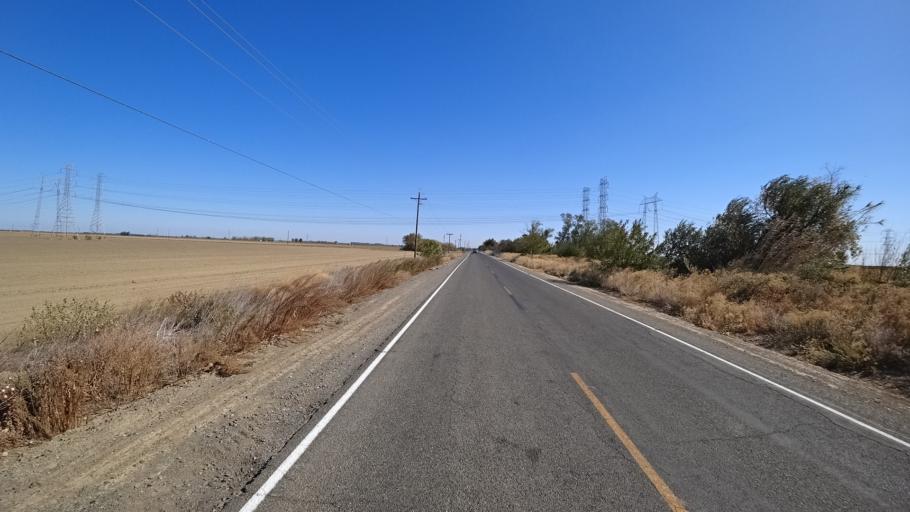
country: US
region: California
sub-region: Yolo County
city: Winters
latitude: 38.5620
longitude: -121.9283
